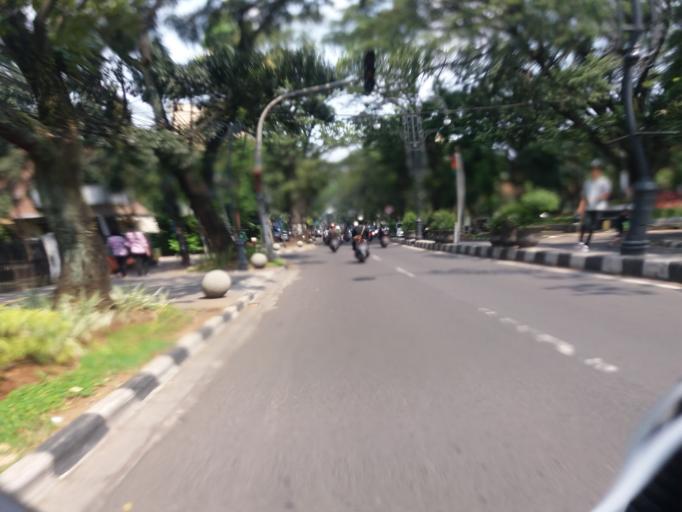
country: ID
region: West Java
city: Bandung
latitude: -6.9023
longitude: 107.6117
